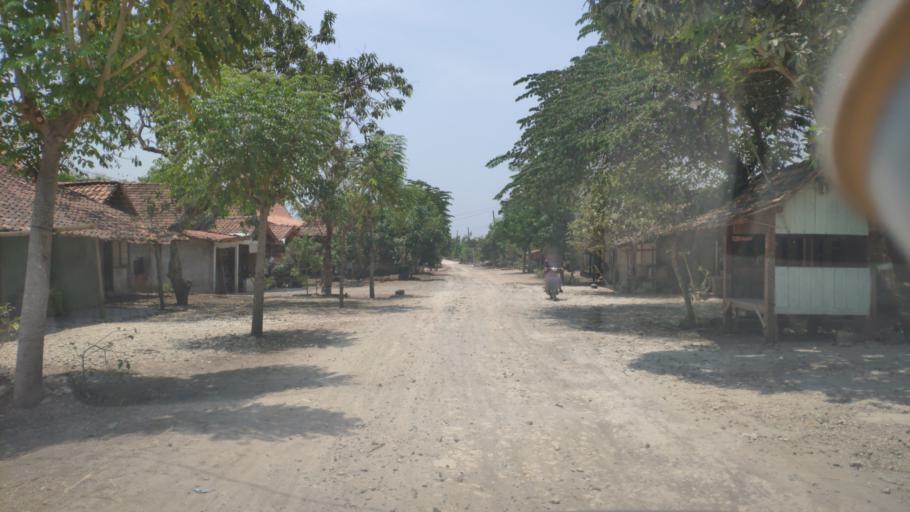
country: ID
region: Central Java
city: Pipes
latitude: -7.1732
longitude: 111.2556
